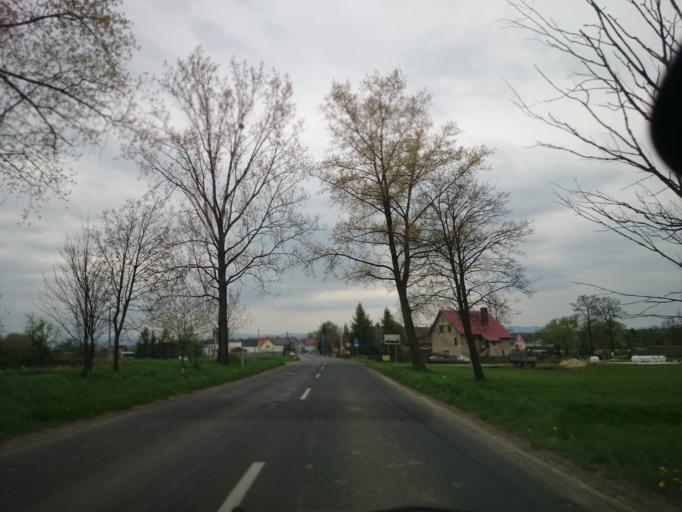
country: PL
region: Opole Voivodeship
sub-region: Powiat nyski
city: Nysa
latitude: 50.4148
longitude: 17.3377
